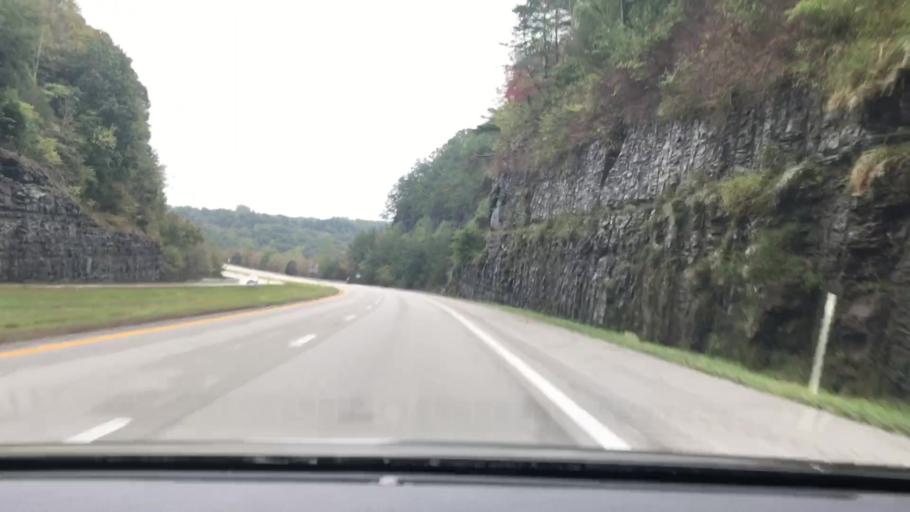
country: US
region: Kentucky
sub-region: Russell County
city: Russell Springs
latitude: 37.0863
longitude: -84.8936
